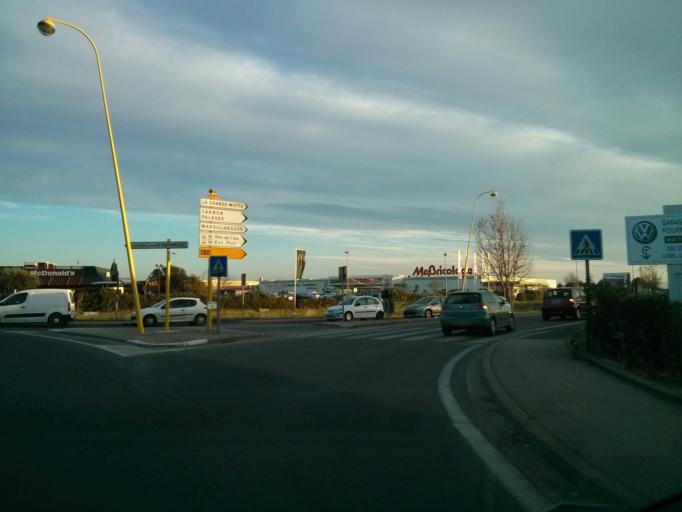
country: FR
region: Languedoc-Roussillon
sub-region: Departement de l'Herault
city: Lunel
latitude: 43.6830
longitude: 4.1501
